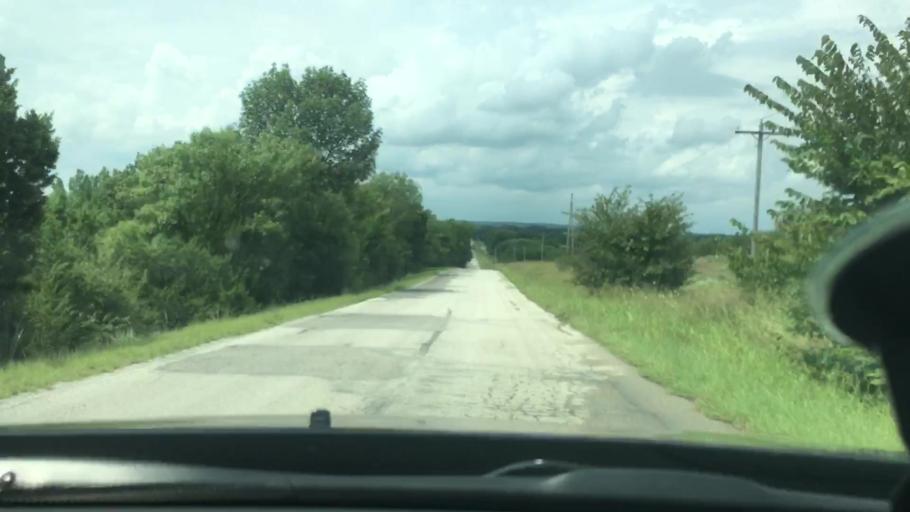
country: US
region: Oklahoma
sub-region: Carter County
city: Dickson
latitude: 34.2527
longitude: -96.9382
